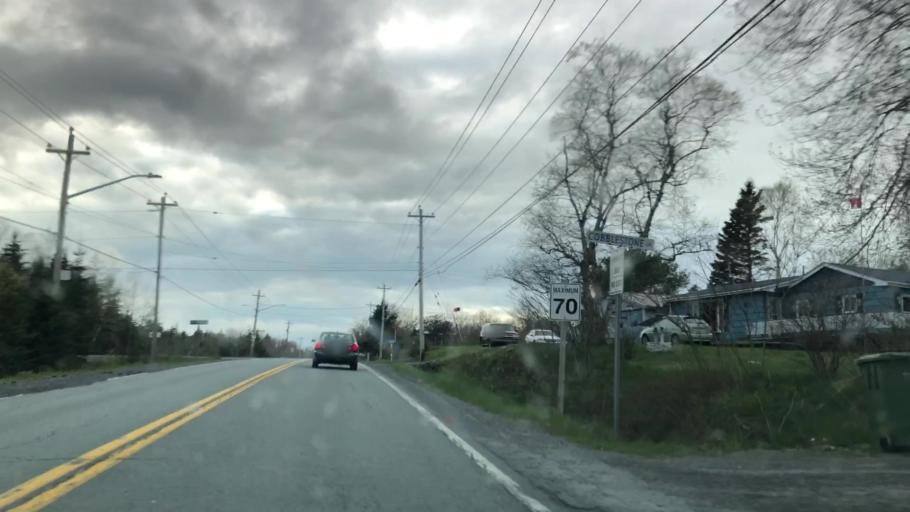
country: CA
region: Nova Scotia
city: Cole Harbour
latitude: 44.7837
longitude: -63.1656
